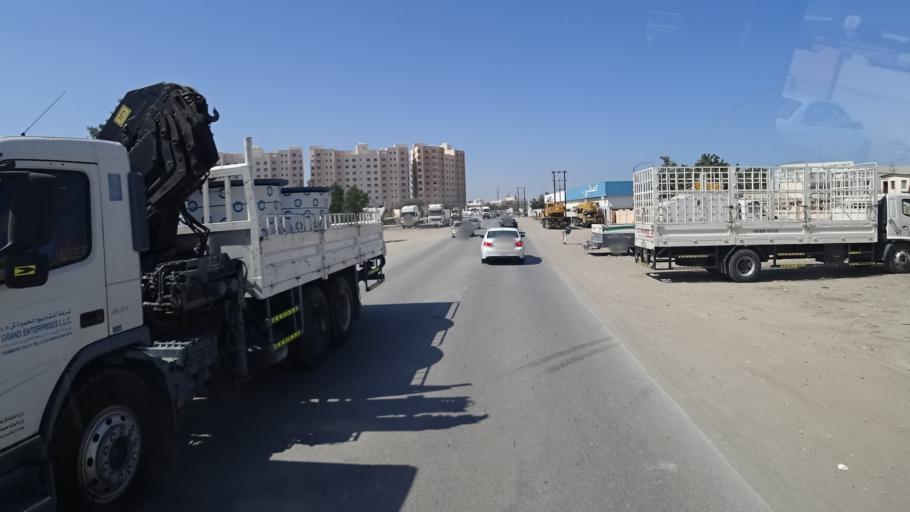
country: OM
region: Muhafazat Masqat
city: Bawshar
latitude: 23.5755
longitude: 58.3694
